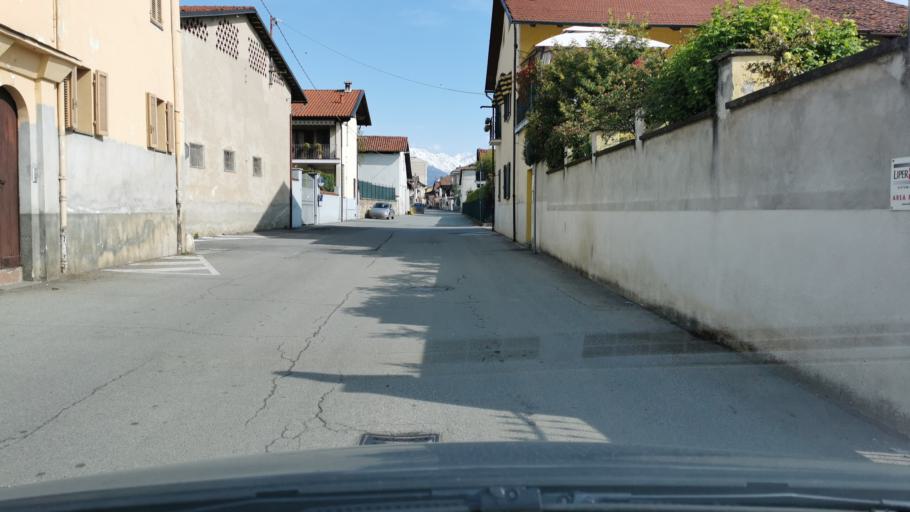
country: IT
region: Piedmont
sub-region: Provincia di Torino
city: Favria
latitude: 45.3271
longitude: 7.6914
